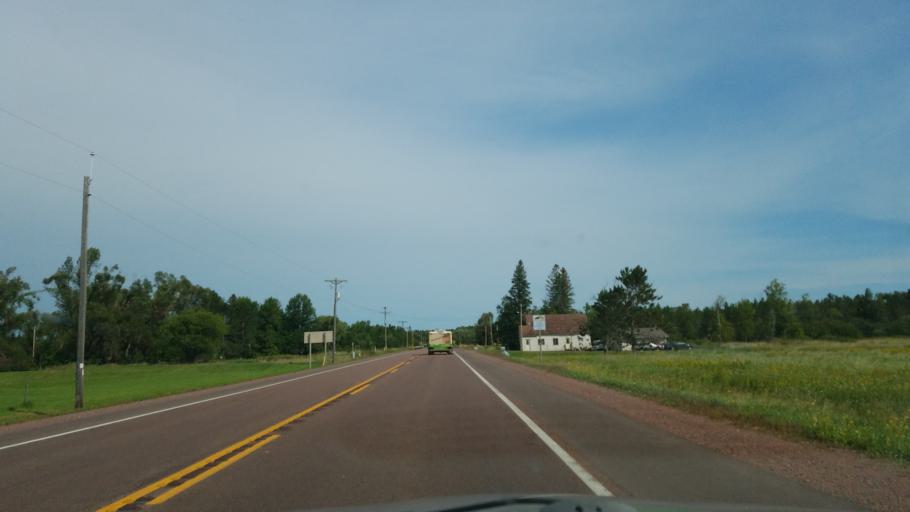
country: US
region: Wisconsin
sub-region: Ashland County
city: Ashland
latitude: 46.5929
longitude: -90.9551
